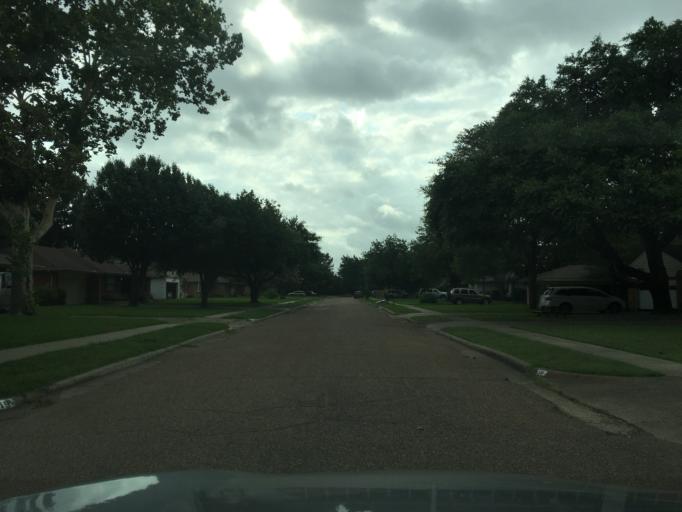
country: US
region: Texas
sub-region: Dallas County
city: Richardson
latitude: 32.9464
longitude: -96.7211
